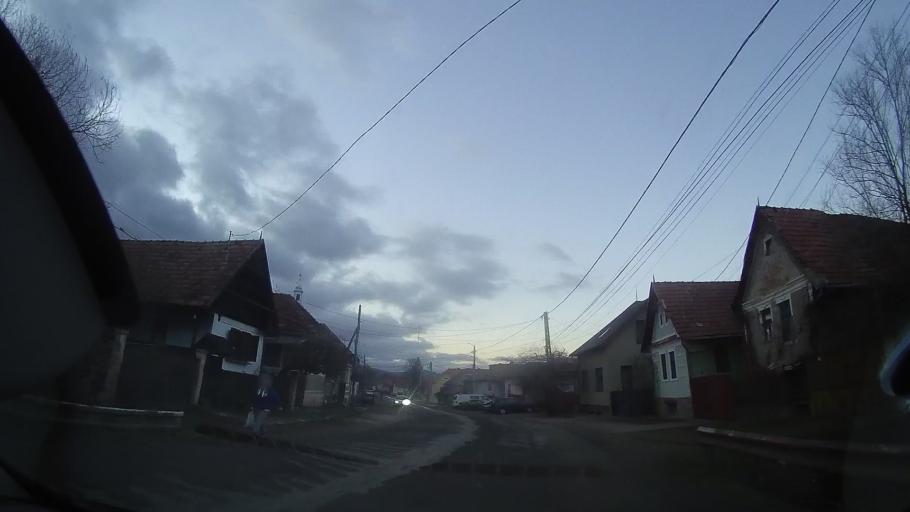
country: RO
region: Cluj
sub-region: Comuna Capusu Mare
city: Capusu Mare
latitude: 46.7915
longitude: 23.2907
